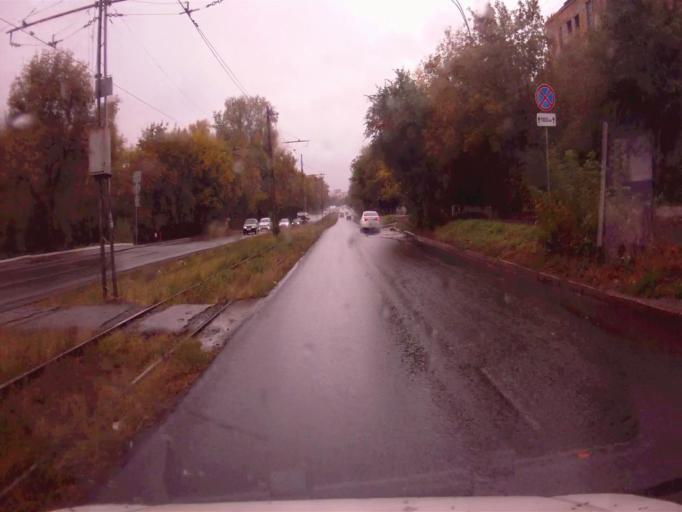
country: RU
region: Chelyabinsk
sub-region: Gorod Chelyabinsk
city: Chelyabinsk
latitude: 55.1780
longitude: 61.4148
